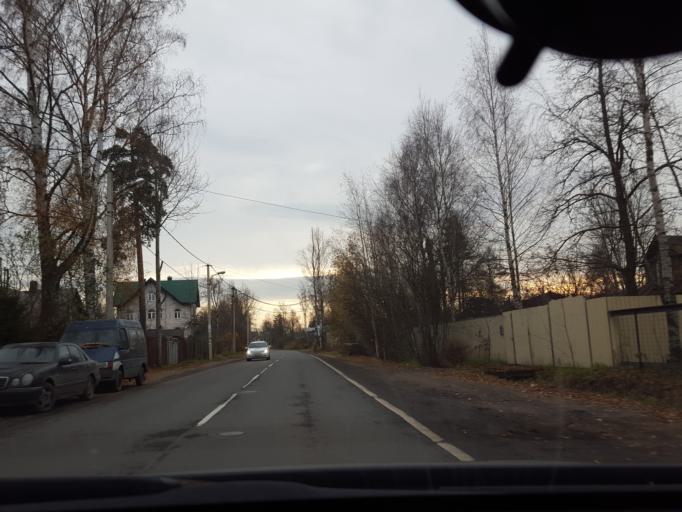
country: RU
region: St.-Petersburg
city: Shuvalovo
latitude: 60.0481
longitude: 30.2948
